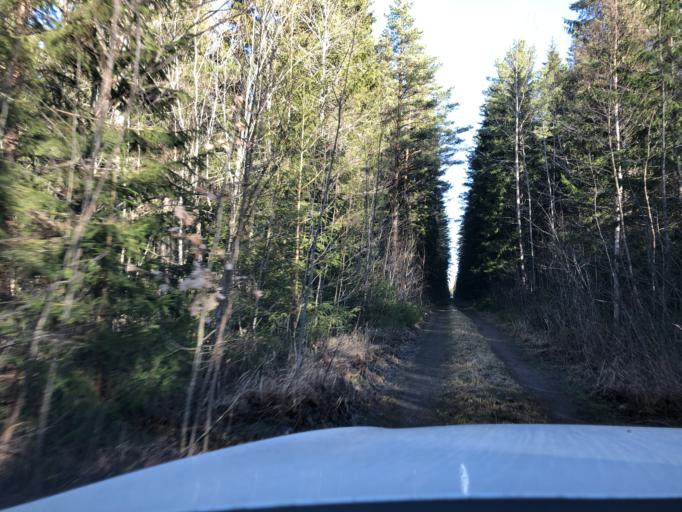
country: SE
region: Gaevleborg
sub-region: Gavle Kommun
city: Hedesunda
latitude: 60.2979
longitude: 16.8986
